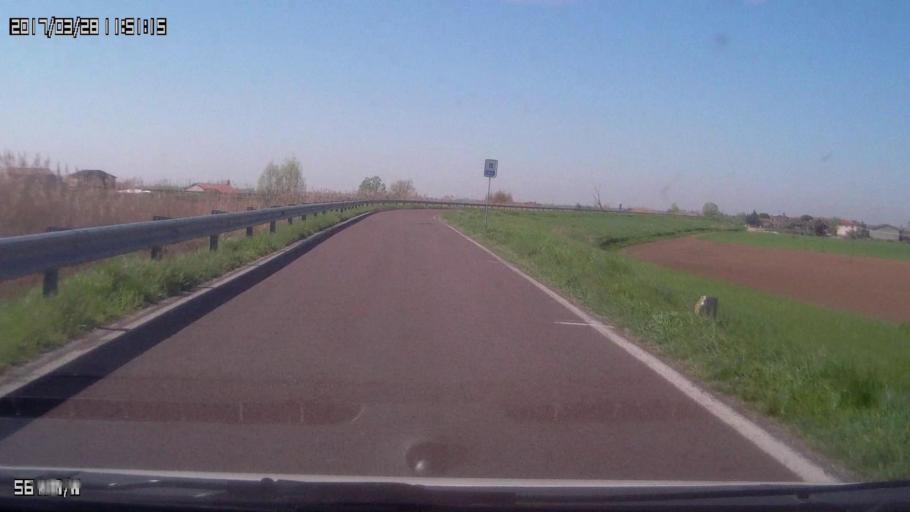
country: IT
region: Veneto
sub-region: Provincia di Venezia
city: Boscochiaro
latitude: 45.1495
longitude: 12.1944
